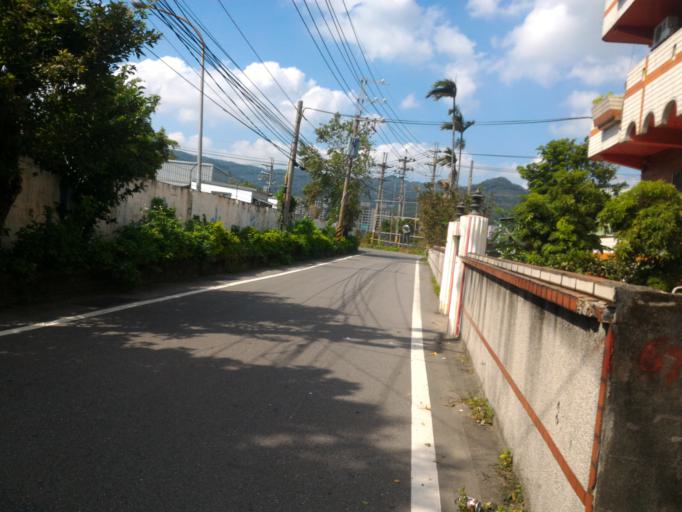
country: TW
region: Taipei
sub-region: Taipei
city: Banqiao
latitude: 24.9642
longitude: 121.3997
